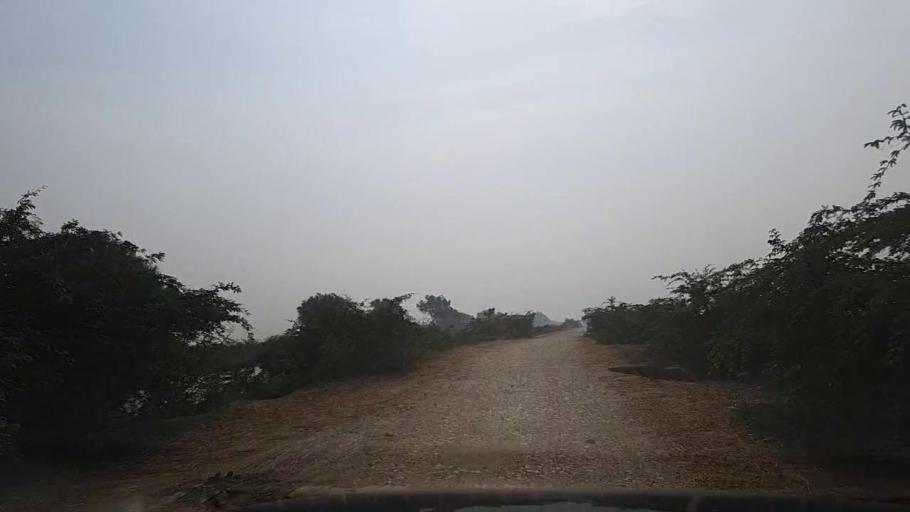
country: PK
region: Sindh
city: Mirpur Sakro
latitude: 24.3751
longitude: 67.7558
